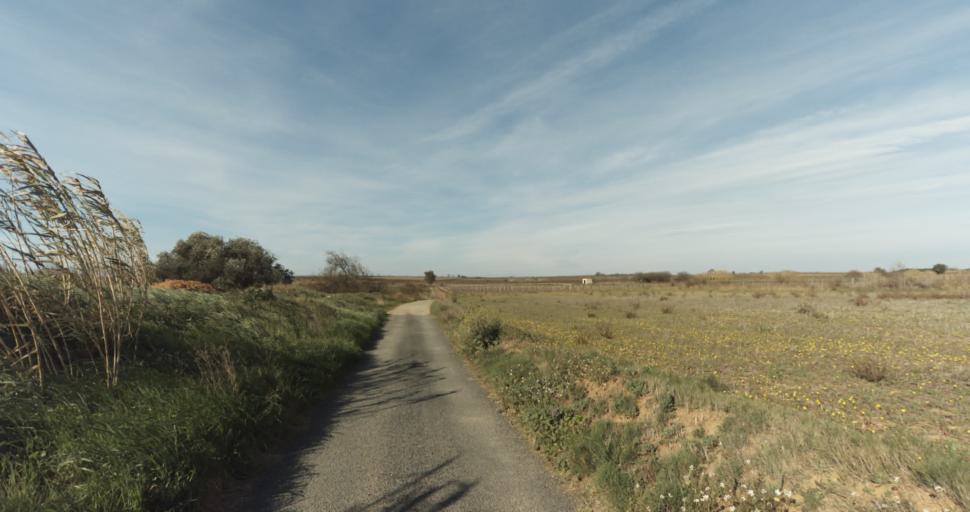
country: FR
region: Languedoc-Roussillon
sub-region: Departement de l'Herault
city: Marseillan
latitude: 43.3610
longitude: 3.5099
